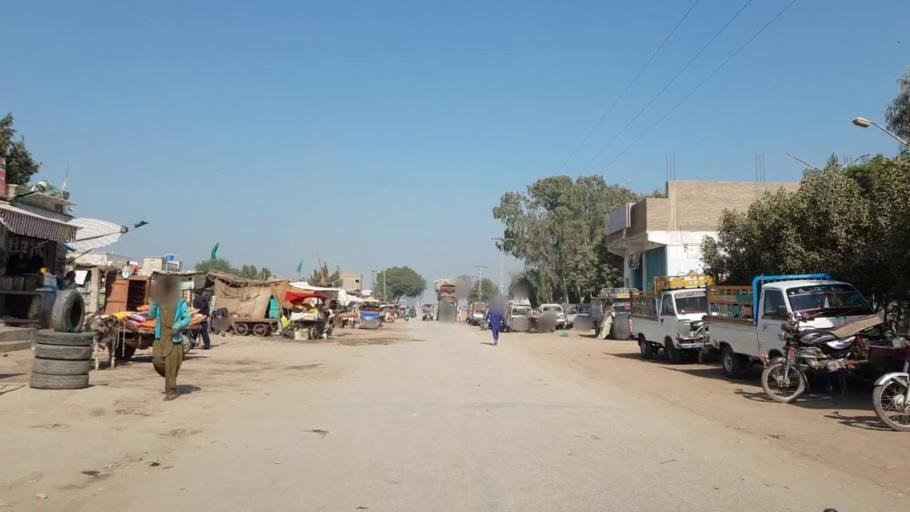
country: PK
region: Sindh
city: Tando Adam
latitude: 25.6348
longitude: 68.5944
